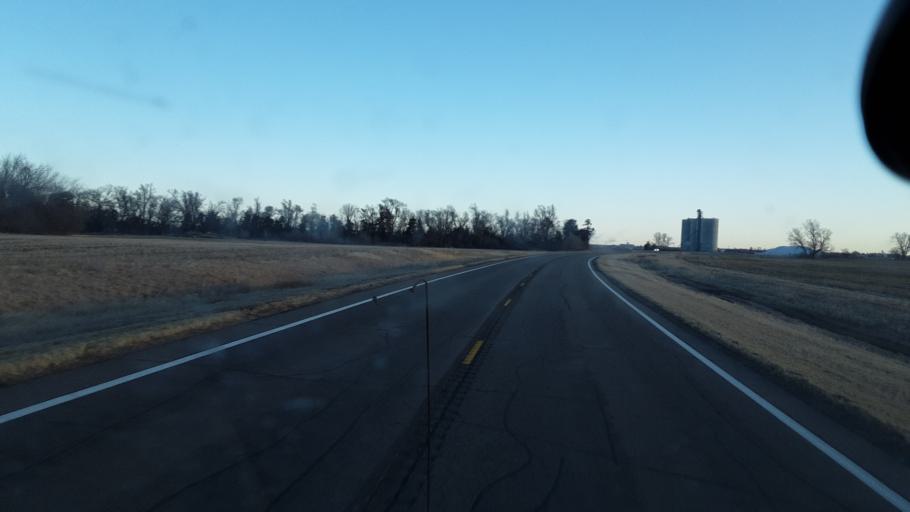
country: US
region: Kansas
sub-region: Rice County
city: Sterling
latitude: 38.2576
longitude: -98.2058
